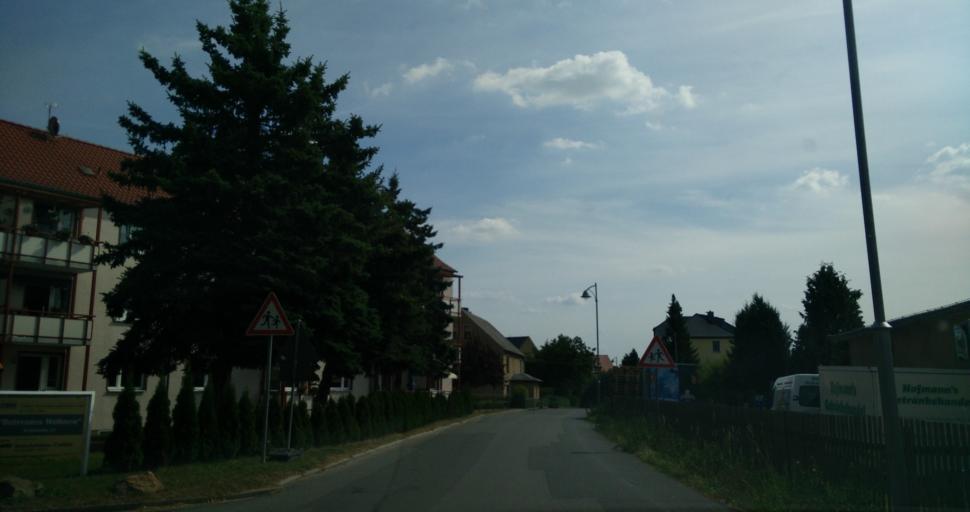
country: DE
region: Saxony
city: Colditz
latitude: 51.1274
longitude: 12.7924
